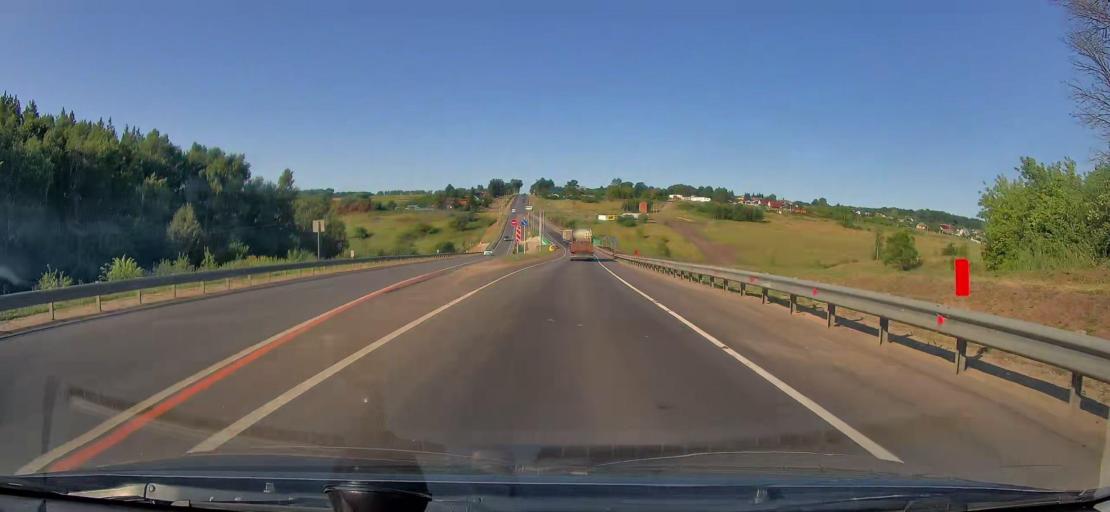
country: RU
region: Orjol
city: Mtsensk
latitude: 53.1889
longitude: 36.4211
